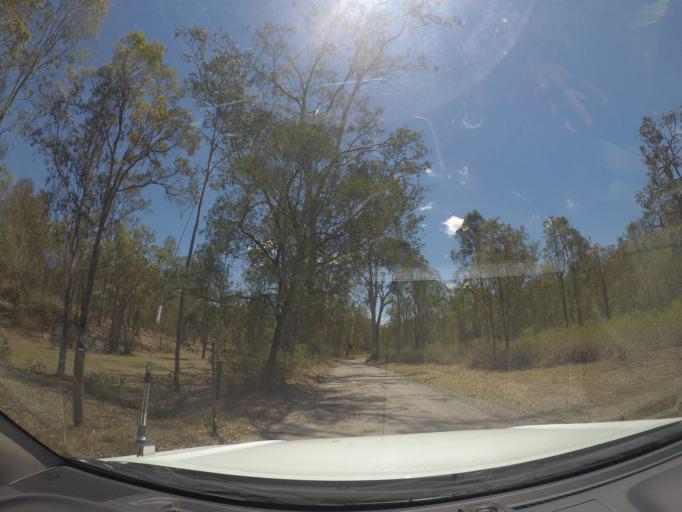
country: AU
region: Queensland
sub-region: Ipswich
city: Redbank Plains
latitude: -27.7568
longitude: 152.8360
